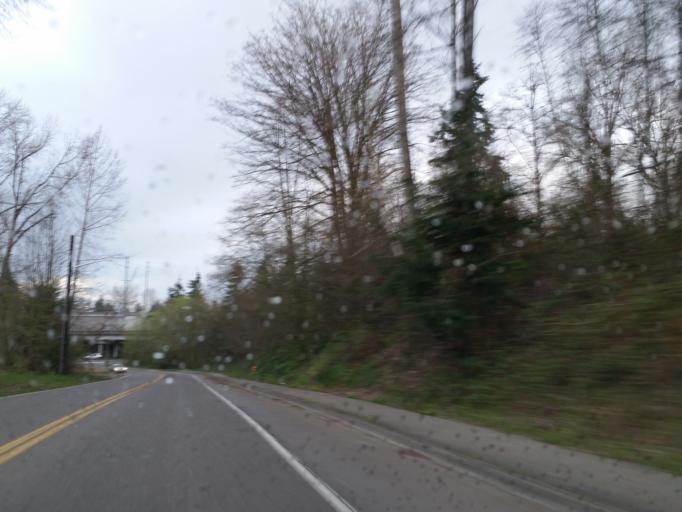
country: US
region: Washington
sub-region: Snohomish County
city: Alderwood Manor
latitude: 47.8137
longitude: -122.2895
